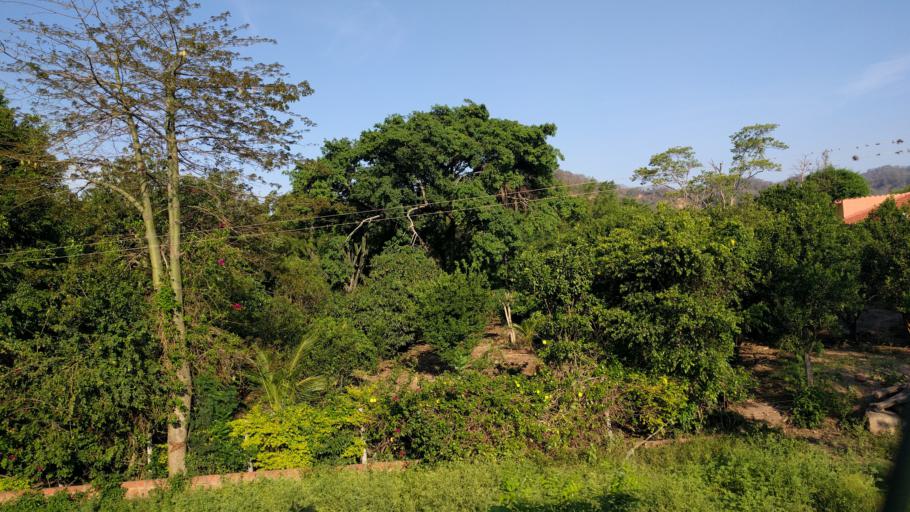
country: BO
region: Santa Cruz
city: Jorochito
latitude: -18.1098
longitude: -63.4581
